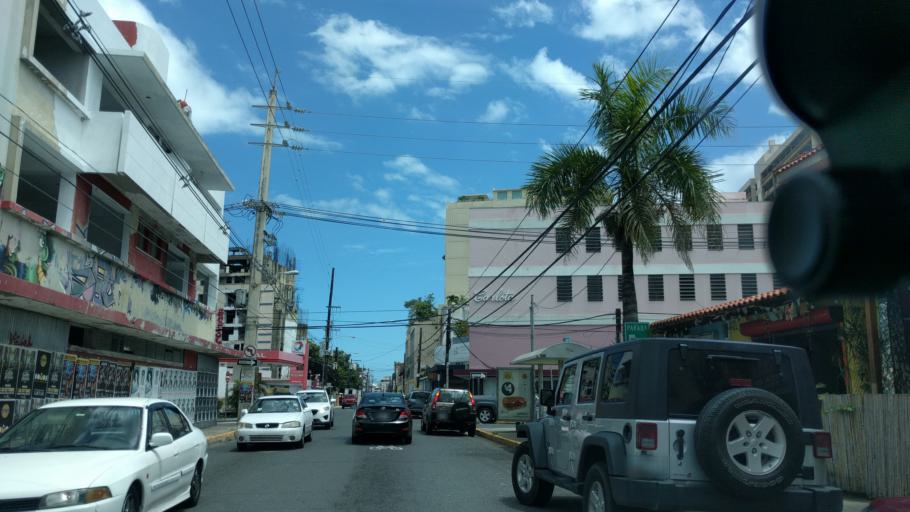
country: PR
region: San Juan
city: San Juan
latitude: 18.4517
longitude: -66.0612
